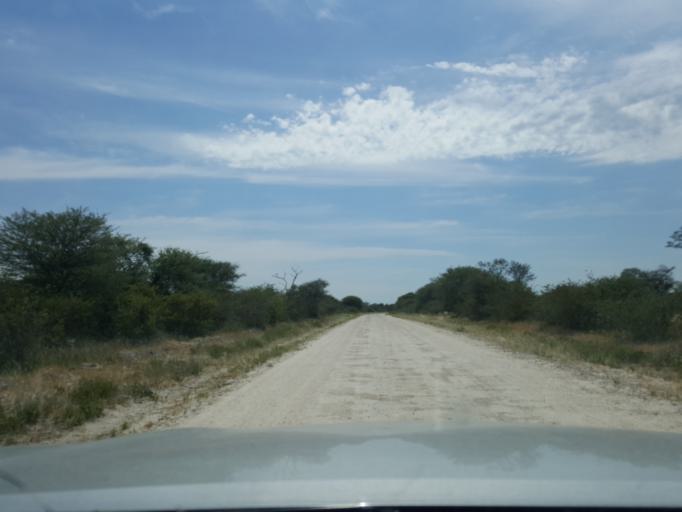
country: BW
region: North West
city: Shakawe
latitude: -18.6828
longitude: 21.8937
